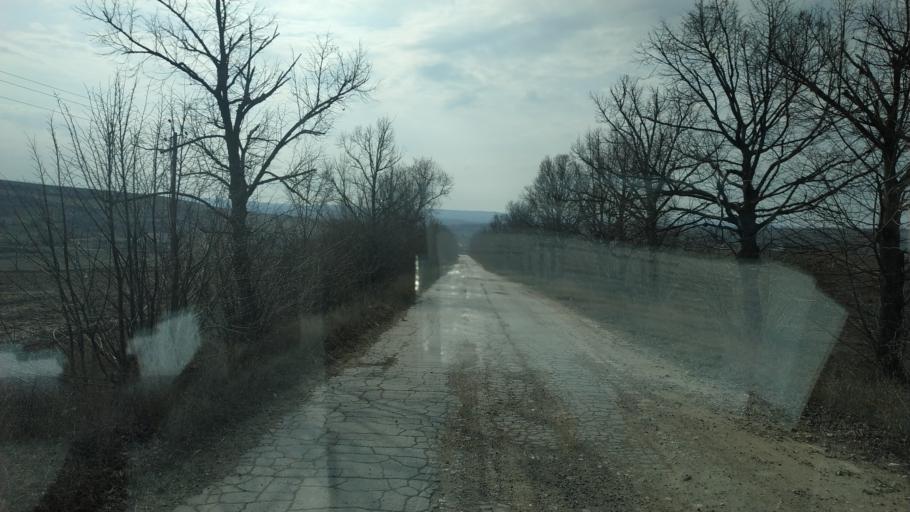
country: MD
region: Anenii Noi
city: Anenii Noi
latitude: 46.9377
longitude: 29.1084
